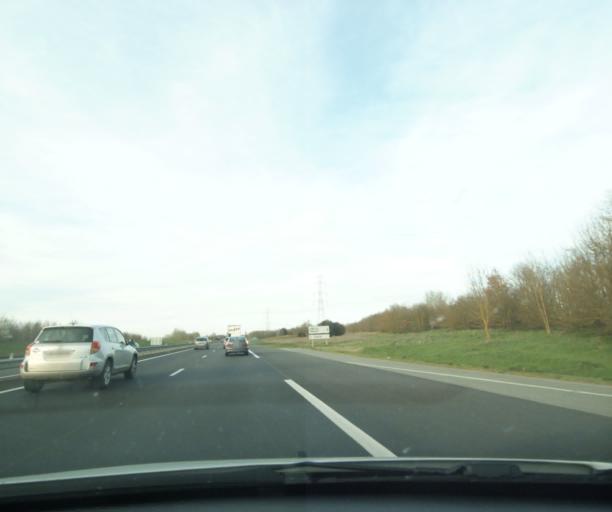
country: FR
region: Midi-Pyrenees
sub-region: Departement de la Haute-Garonne
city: Seysses
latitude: 43.4835
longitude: 1.3276
